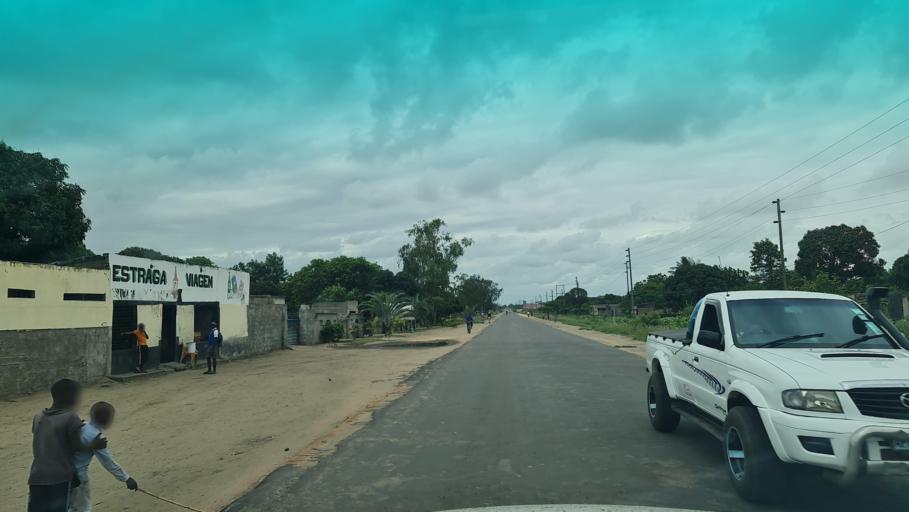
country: MZ
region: Maputo
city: Manhica
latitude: -25.4400
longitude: 32.7735
